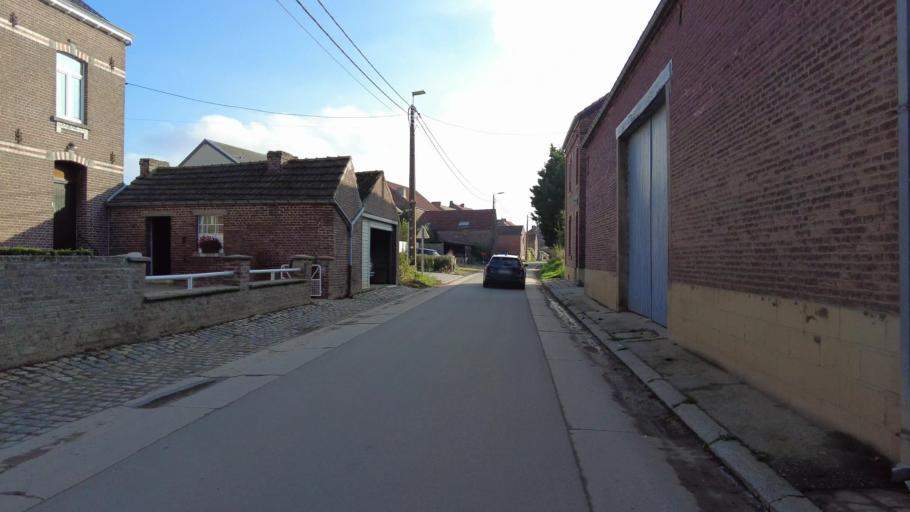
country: BE
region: Wallonia
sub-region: Province du Brabant Wallon
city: Jodoigne
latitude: 50.7393
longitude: 4.8988
